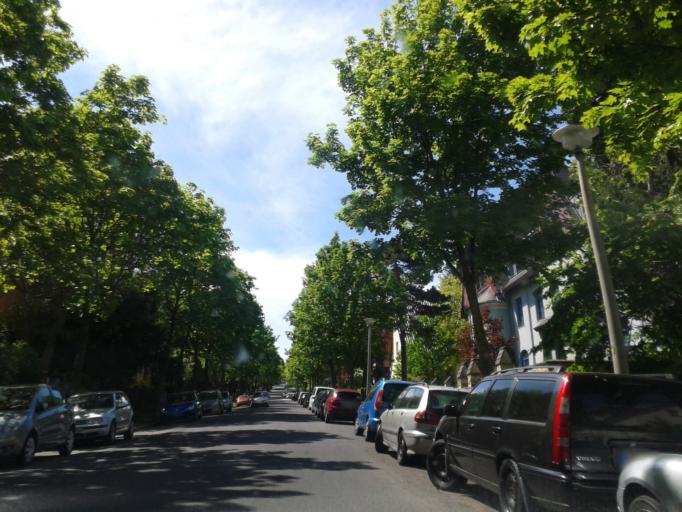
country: DE
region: Saxony
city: Dresden
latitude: 51.0272
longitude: 13.7135
